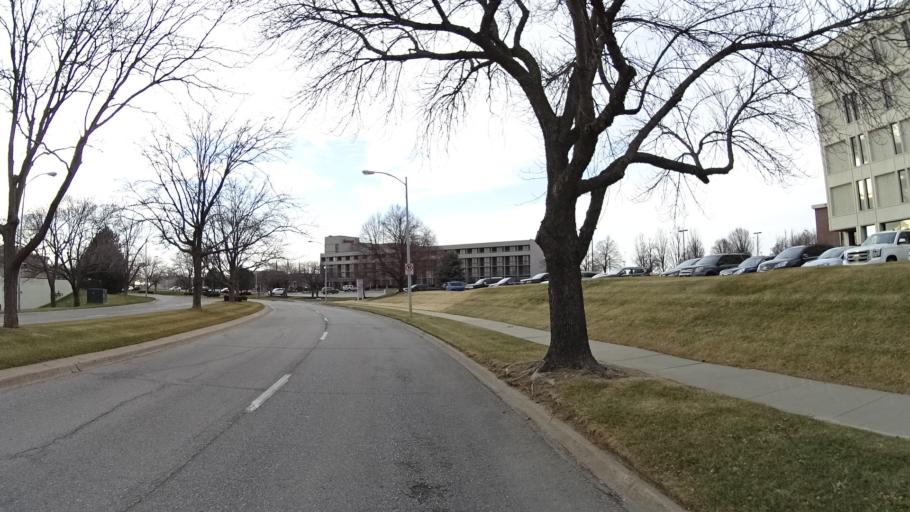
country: US
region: Nebraska
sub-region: Douglas County
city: Ralston
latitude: 41.2610
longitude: -96.0705
